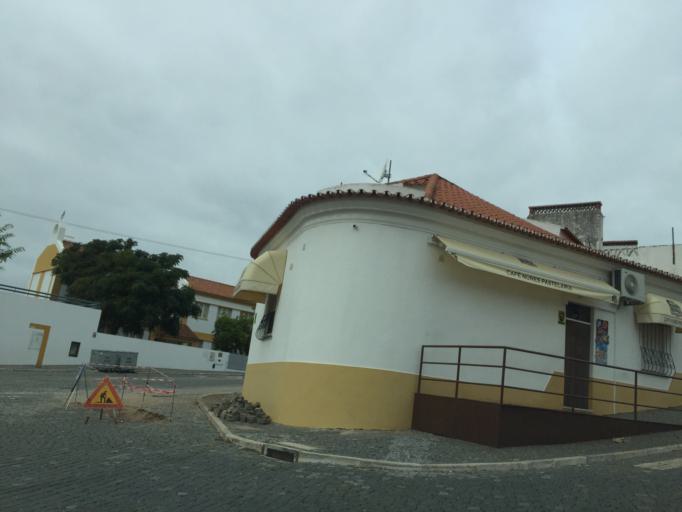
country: PT
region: Portalegre
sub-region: Avis
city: Avis
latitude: 39.0551
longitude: -7.8898
